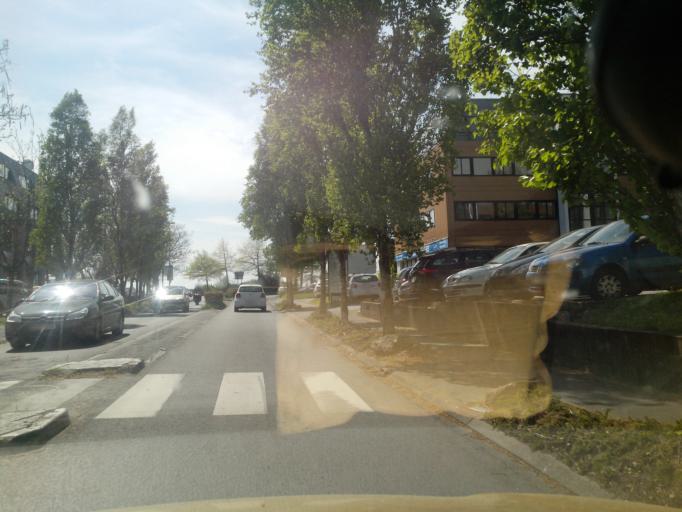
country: FR
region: Pays de la Loire
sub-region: Departement de la Loire-Atlantique
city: Orvault
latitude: 47.2522
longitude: -1.6192
